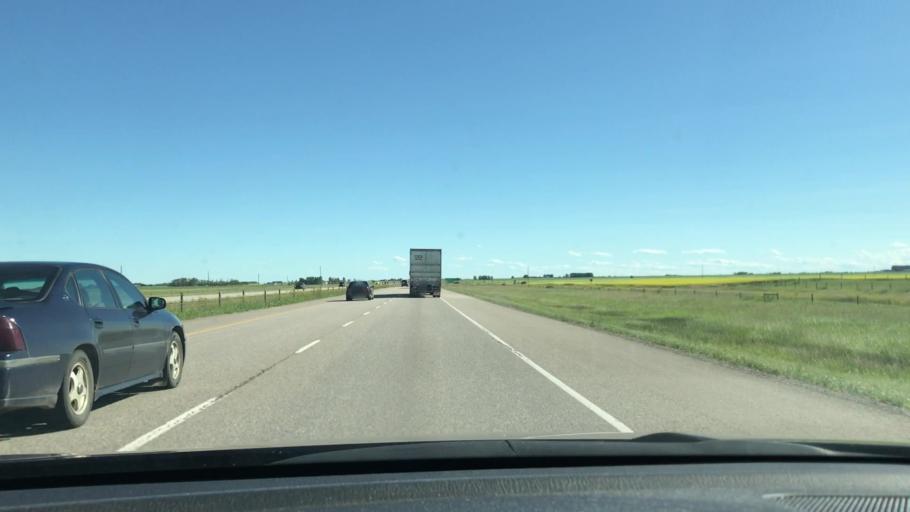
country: CA
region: Alberta
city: Olds
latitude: 51.7122
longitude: -114.0256
